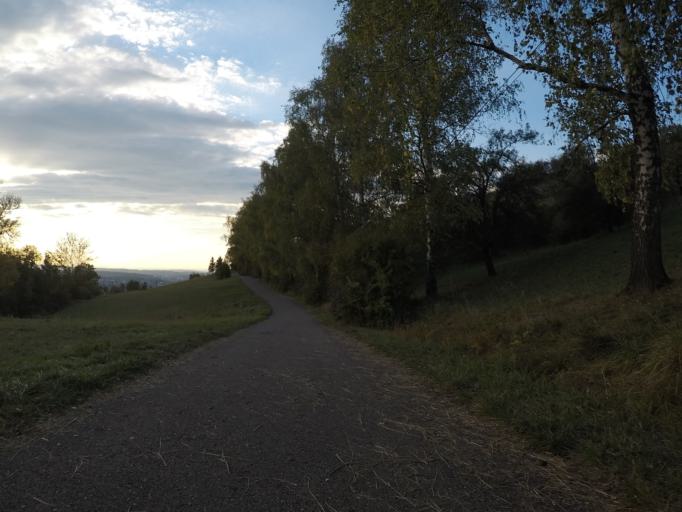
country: DE
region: Baden-Wuerttemberg
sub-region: Tuebingen Region
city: Eningen unter Achalm
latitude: 48.4900
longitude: 9.2433
